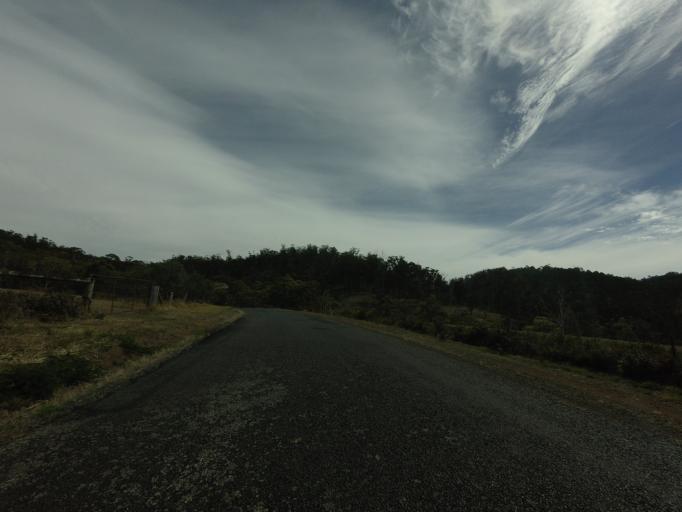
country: AU
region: Tasmania
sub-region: Sorell
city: Sorell
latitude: -42.5709
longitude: 147.6928
